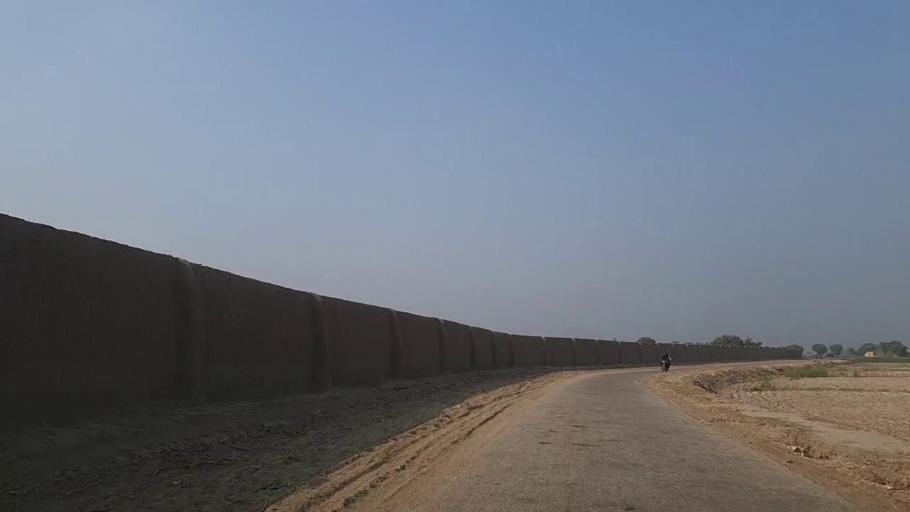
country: PK
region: Sindh
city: Sann
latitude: 26.1075
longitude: 68.1758
